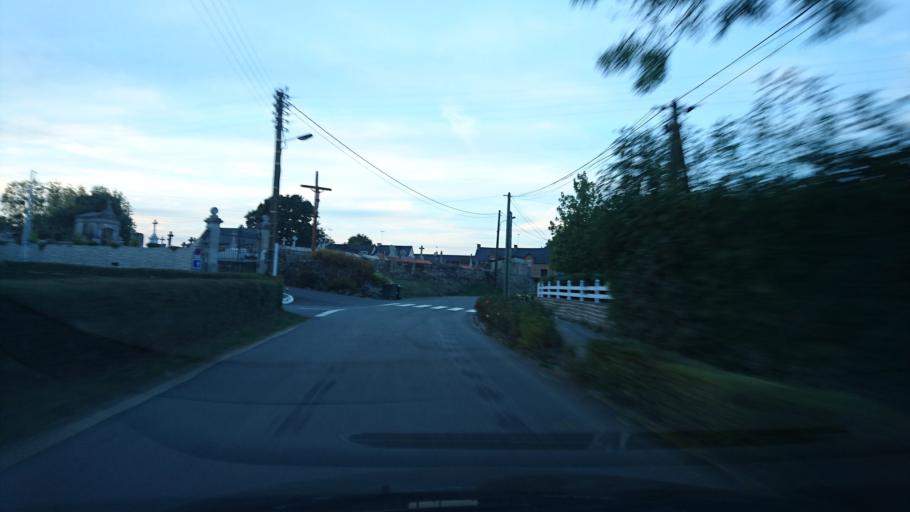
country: FR
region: Brittany
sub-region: Departement d'Ille-et-Vilaine
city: Guignen
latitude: 47.8684
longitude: -1.8869
